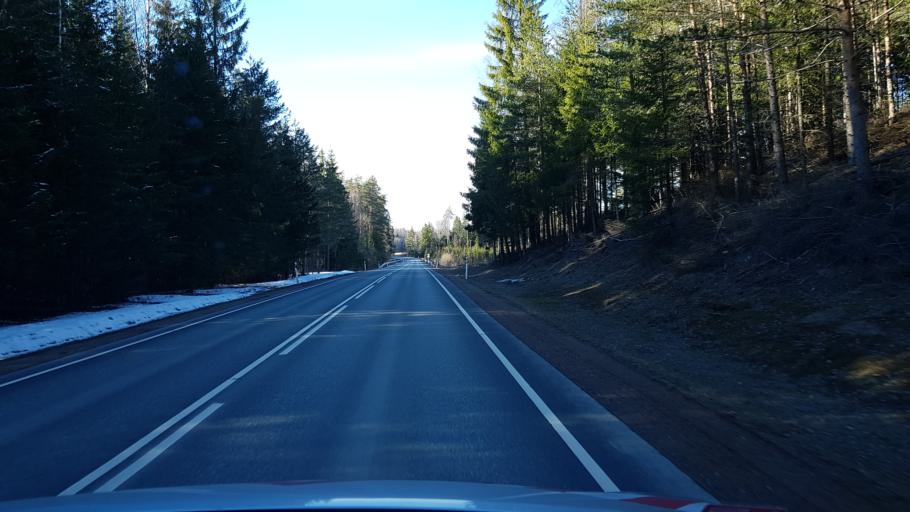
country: EE
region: Laeaene-Virumaa
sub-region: Tapa vald
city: Tapa
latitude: 59.4097
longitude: 26.0017
